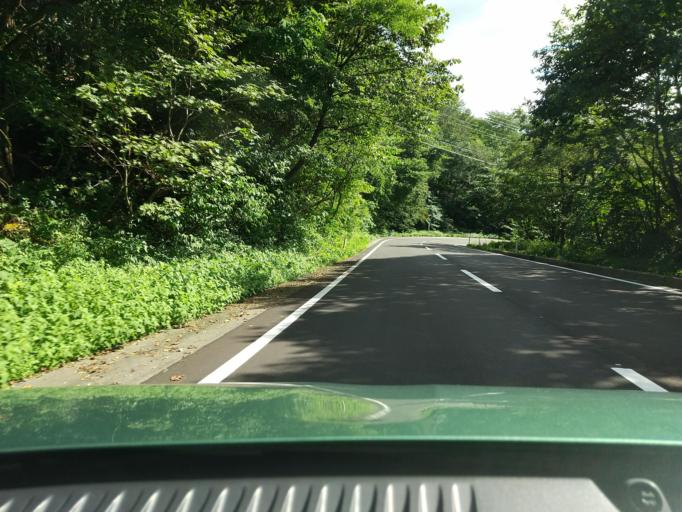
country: JP
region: Iwate
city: Shizukuishi
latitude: 39.7663
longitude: 140.7554
